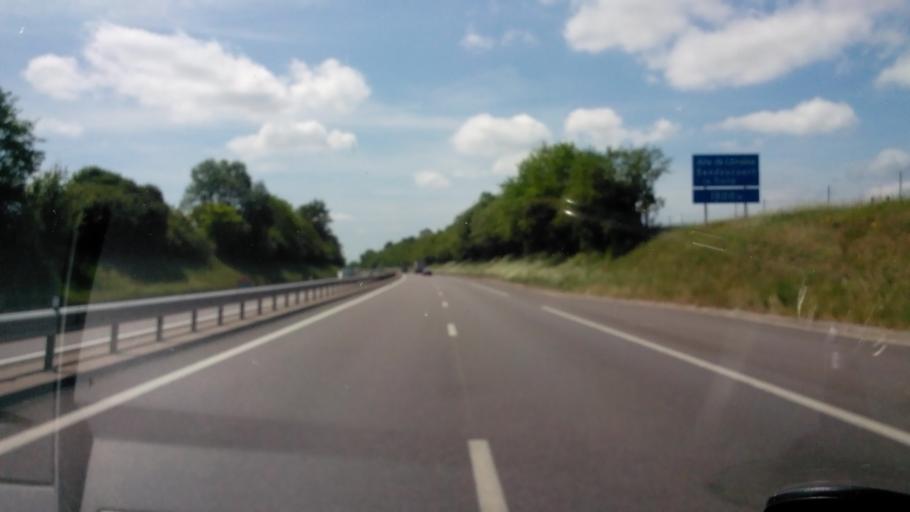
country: FR
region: Lorraine
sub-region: Departement des Vosges
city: Chatenois
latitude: 48.2867
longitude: 5.8556
